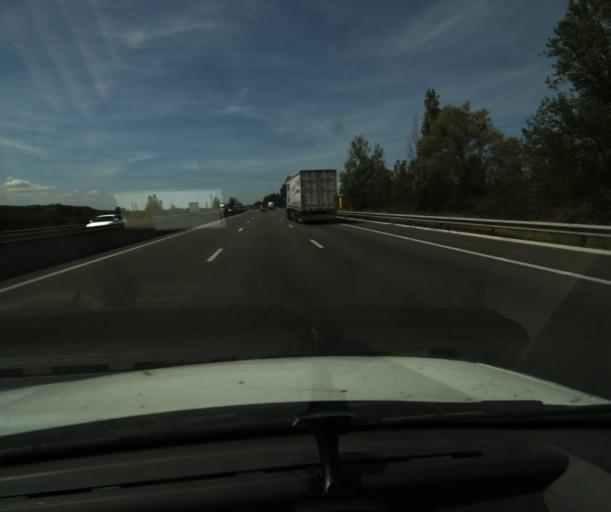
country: FR
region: Midi-Pyrenees
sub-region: Departement de la Haute-Garonne
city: Castanet-Tolosan
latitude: 43.5314
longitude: 1.5140
